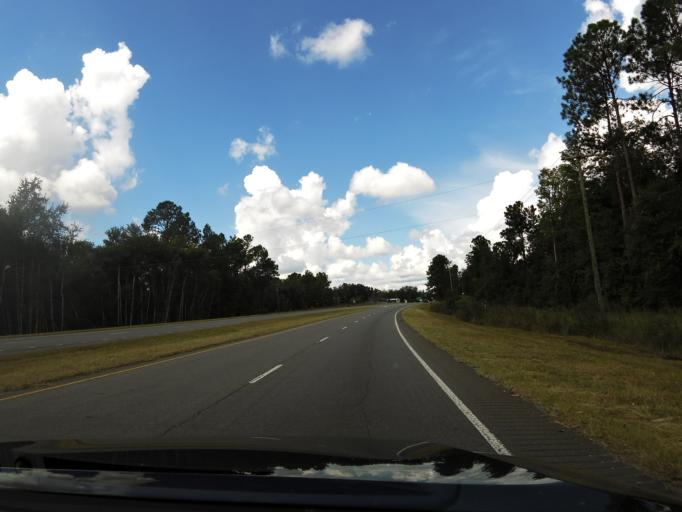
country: US
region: Georgia
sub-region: Charlton County
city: Folkston
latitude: 30.8068
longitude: -81.9951
